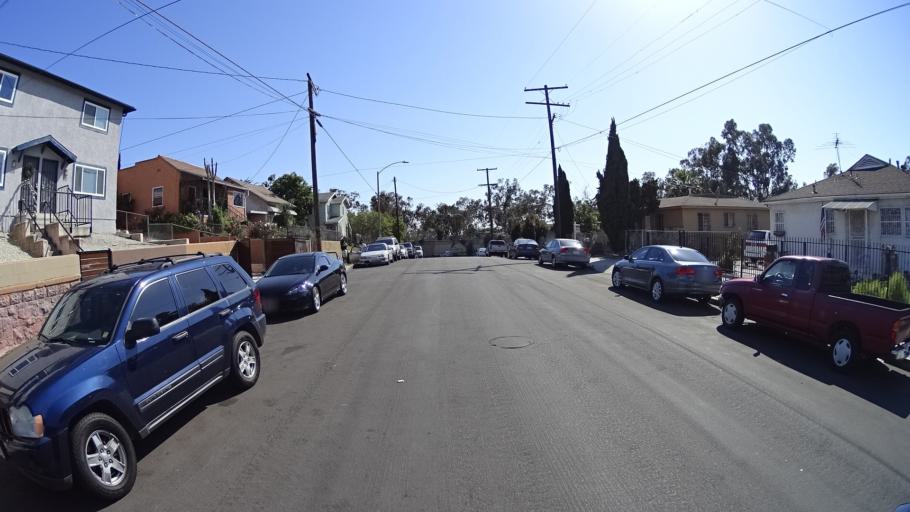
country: US
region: California
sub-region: Los Angeles County
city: Boyle Heights
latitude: 34.0514
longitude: -118.2132
